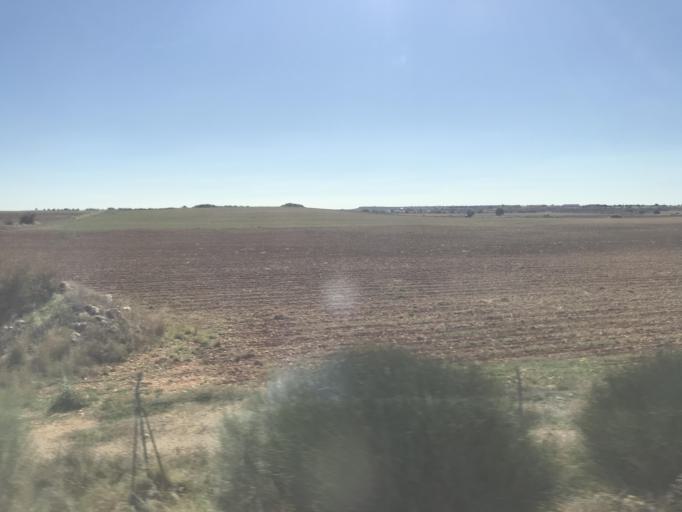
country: ES
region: Castille-La Mancha
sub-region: Provincia de Guadalajara
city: Almadrones
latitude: 40.8715
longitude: -2.7690
